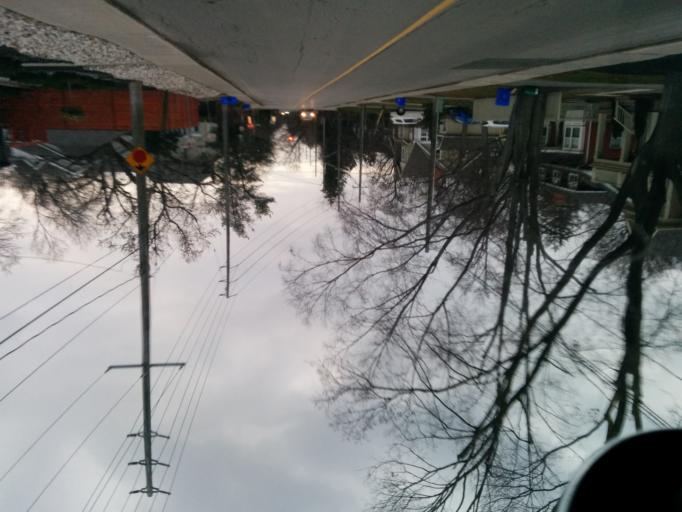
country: CA
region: Ontario
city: Oakville
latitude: 43.4561
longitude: -79.6748
